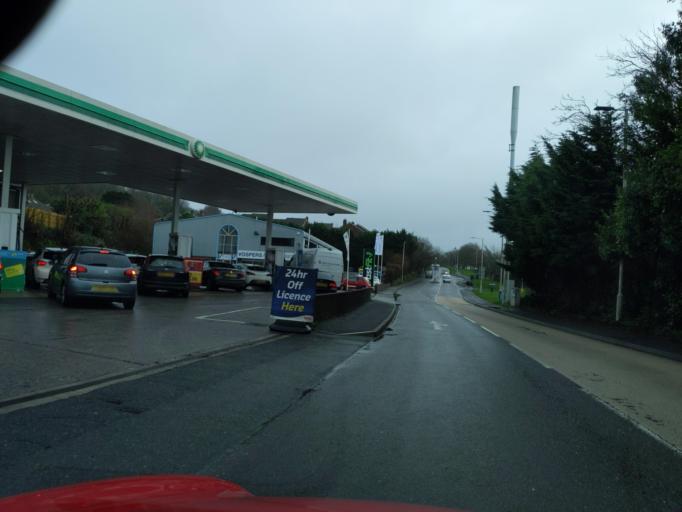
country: GB
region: England
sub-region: Devon
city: Plympton
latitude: 50.3827
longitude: -4.0319
